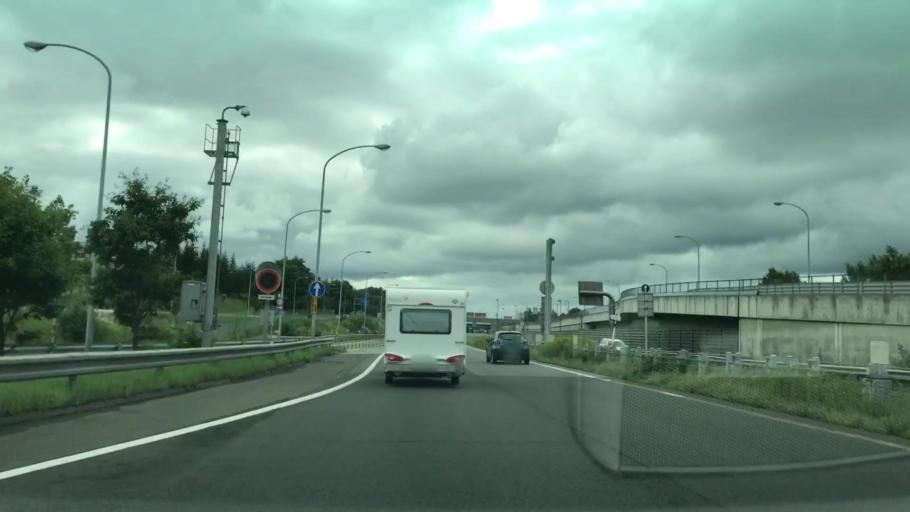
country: JP
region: Hokkaido
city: Kitahiroshima
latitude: 43.0137
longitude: 141.4649
